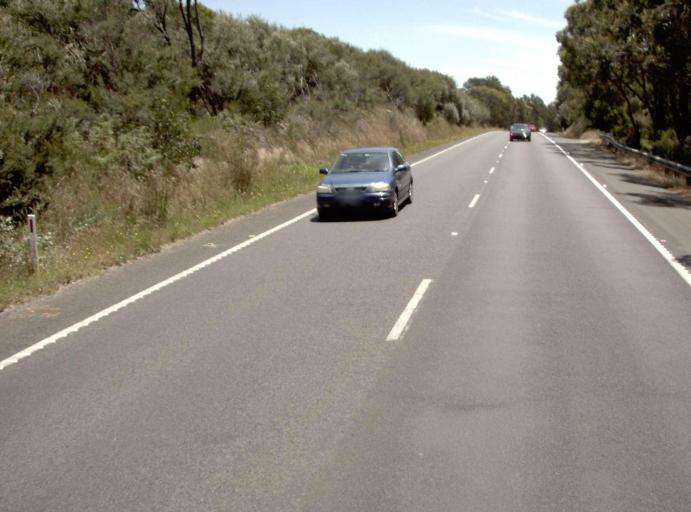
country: AU
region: Victoria
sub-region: Latrobe
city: Moe
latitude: -38.2036
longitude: 146.2970
